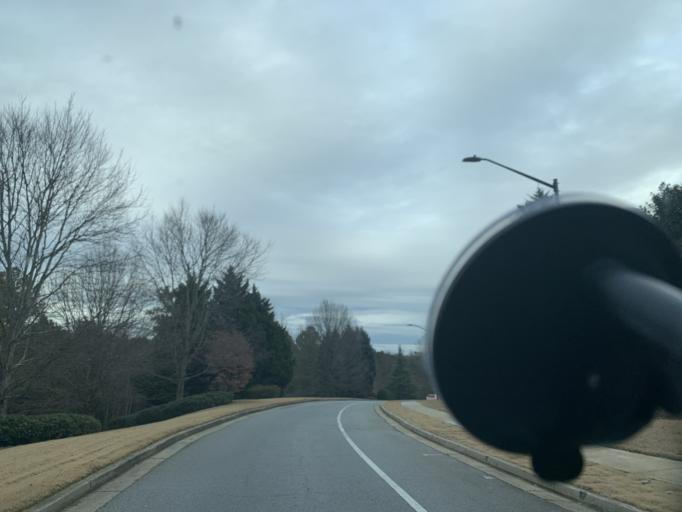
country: US
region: Georgia
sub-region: Cherokee County
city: Woodstock
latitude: 34.0872
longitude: -84.4609
